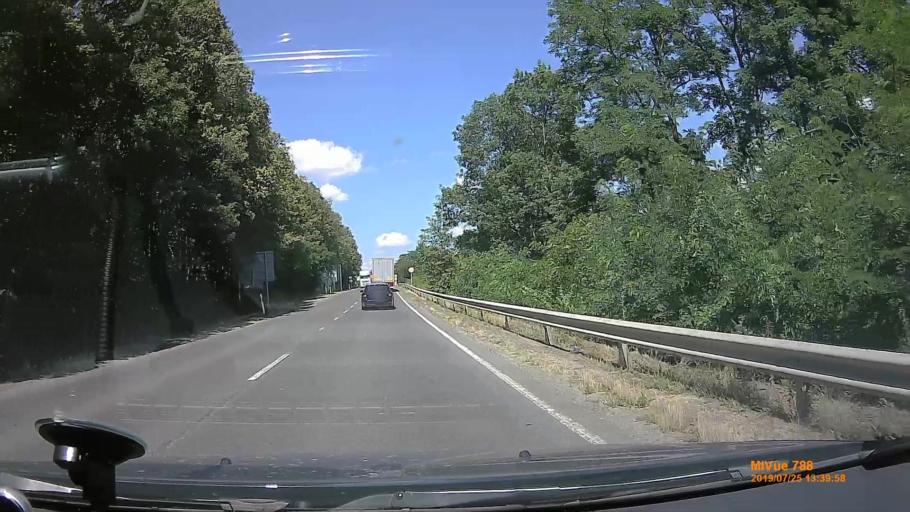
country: HU
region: Borsod-Abauj-Zemplen
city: Gonc
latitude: 48.4324
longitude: 21.1823
